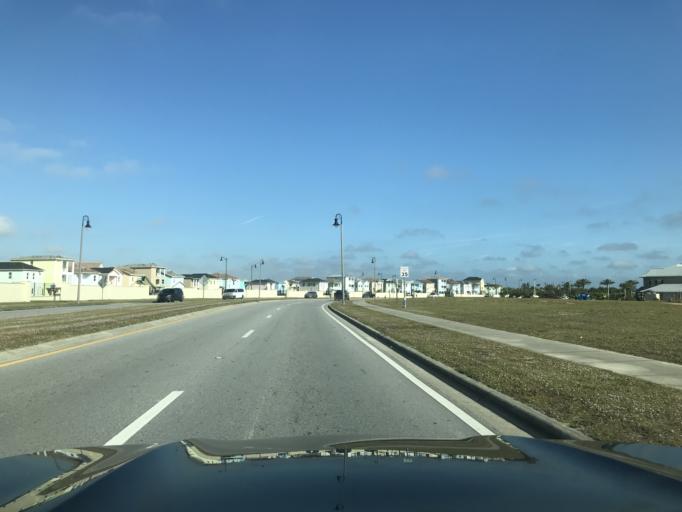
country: US
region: Florida
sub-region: Polk County
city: Citrus Ridge
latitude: 28.3332
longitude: -81.6071
